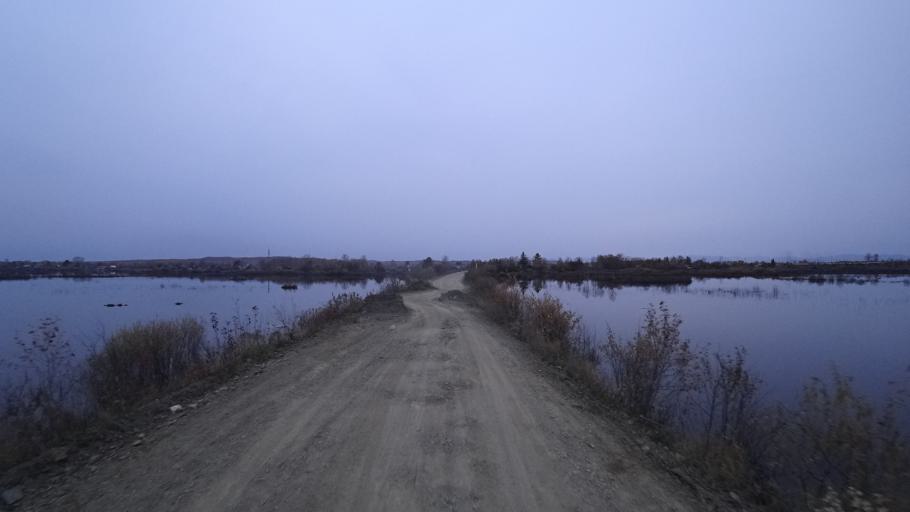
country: RU
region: Khabarovsk Krai
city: Amursk
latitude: 49.8968
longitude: 136.1454
